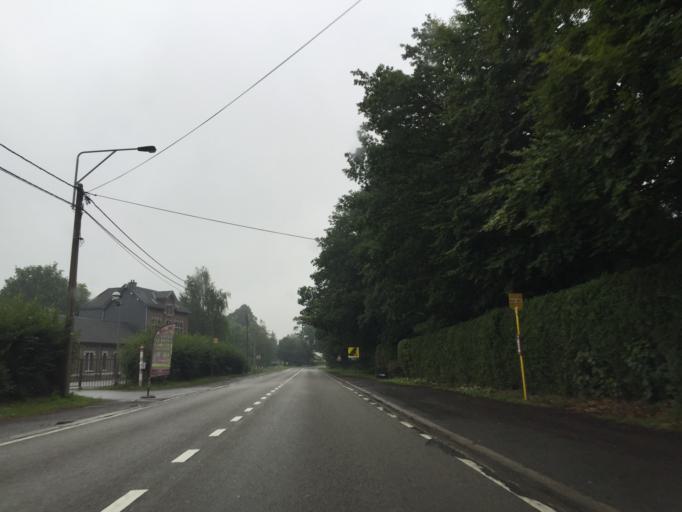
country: BE
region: Wallonia
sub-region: Province de Liege
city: Spa
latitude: 50.5082
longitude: 5.8922
